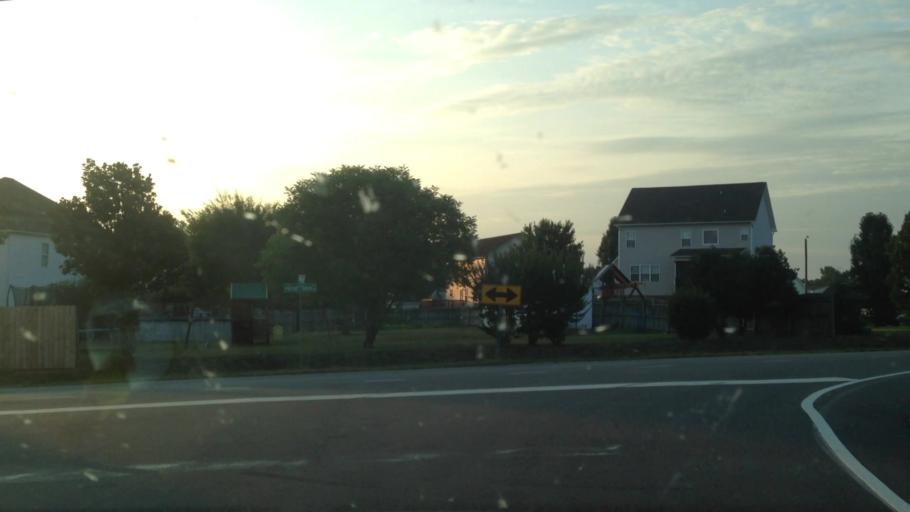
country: US
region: North Carolina
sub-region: Forsyth County
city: Kernersville
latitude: 36.1431
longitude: -80.0819
